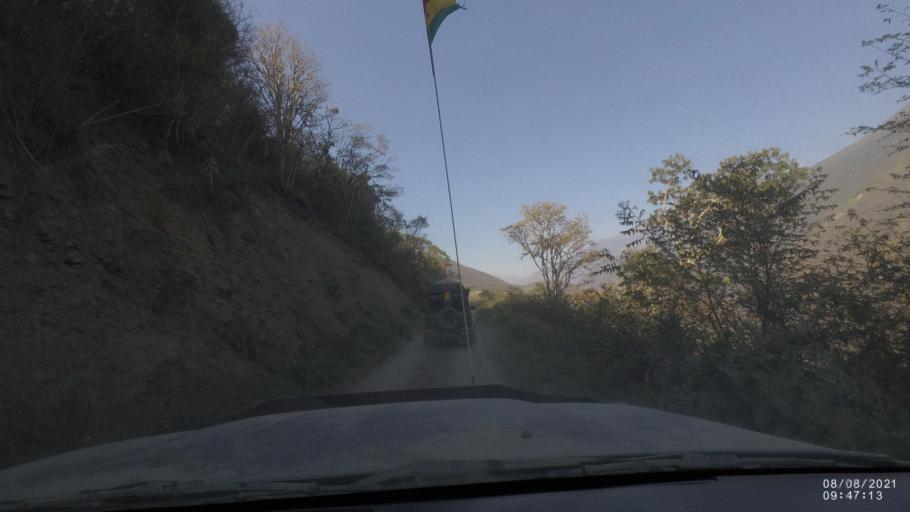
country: BO
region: La Paz
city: Quime
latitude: -16.6083
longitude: -66.7294
